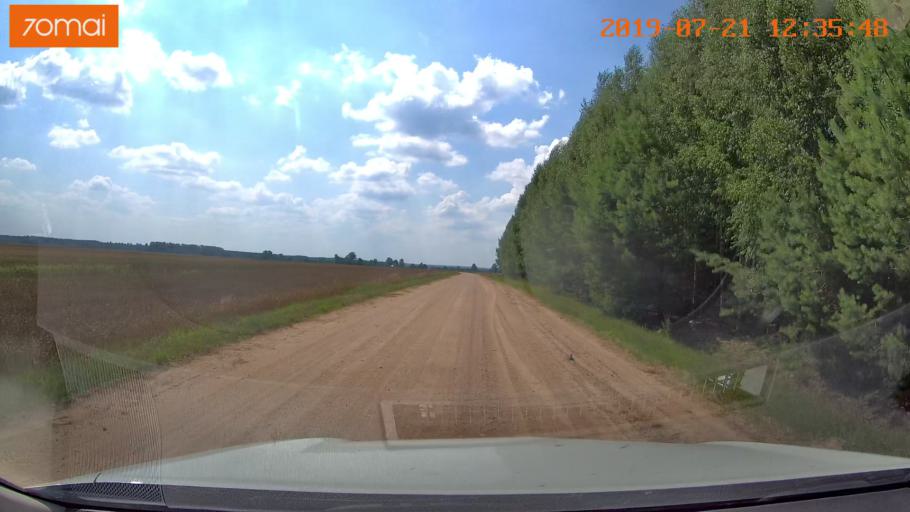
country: BY
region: Grodnenskaya
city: Lyubcha
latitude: 53.8744
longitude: 26.0056
